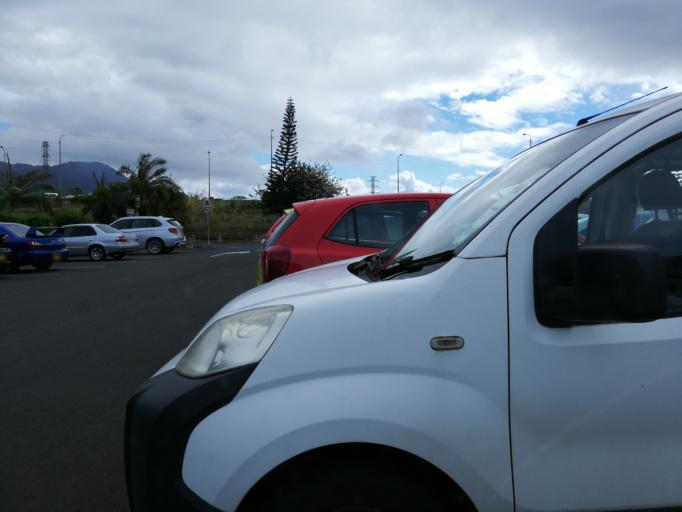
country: MU
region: Plaines Wilhems
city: Ebene
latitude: -20.2437
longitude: 57.4870
